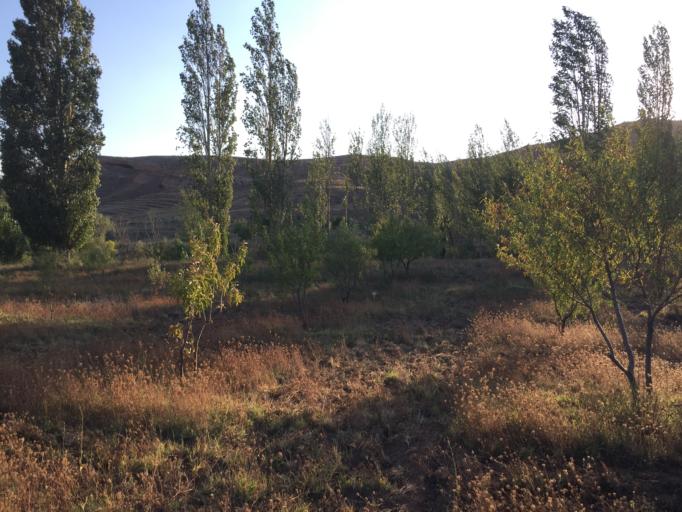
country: TR
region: Nevsehir
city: Hacibektas
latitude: 38.9179
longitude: 34.6300
